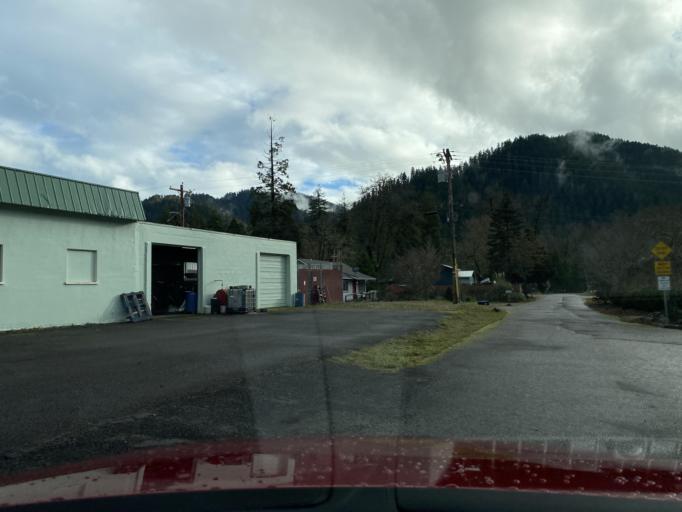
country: US
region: Oregon
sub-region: Lane County
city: Oakridge
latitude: 43.7471
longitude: -122.4925
